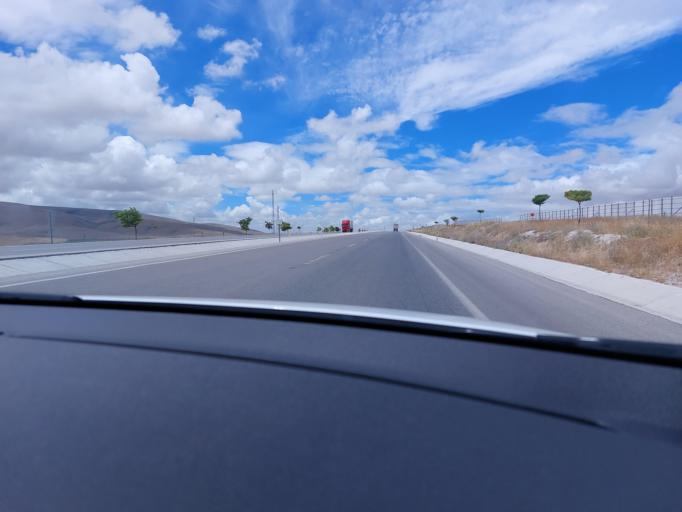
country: TR
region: Konya
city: Obruk
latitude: 38.0610
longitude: 33.0399
